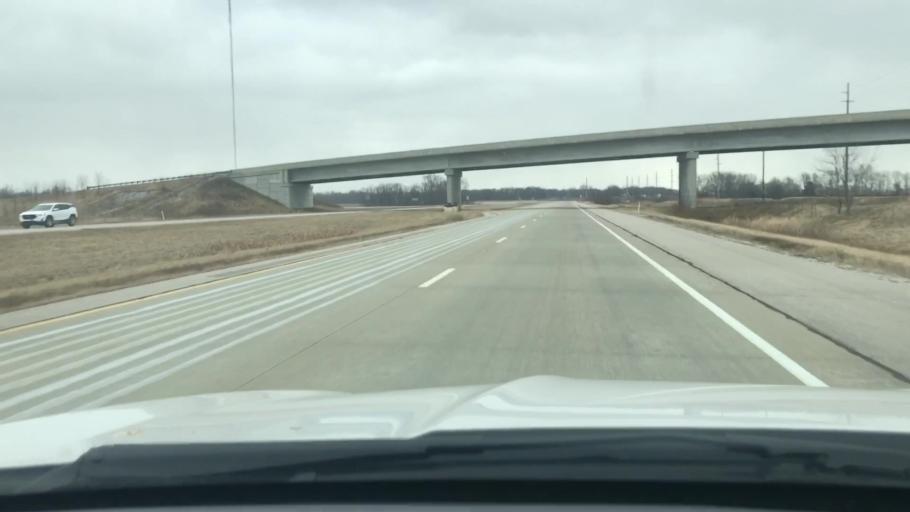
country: US
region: Indiana
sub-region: Carroll County
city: Delphi
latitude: 40.4992
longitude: -86.7342
